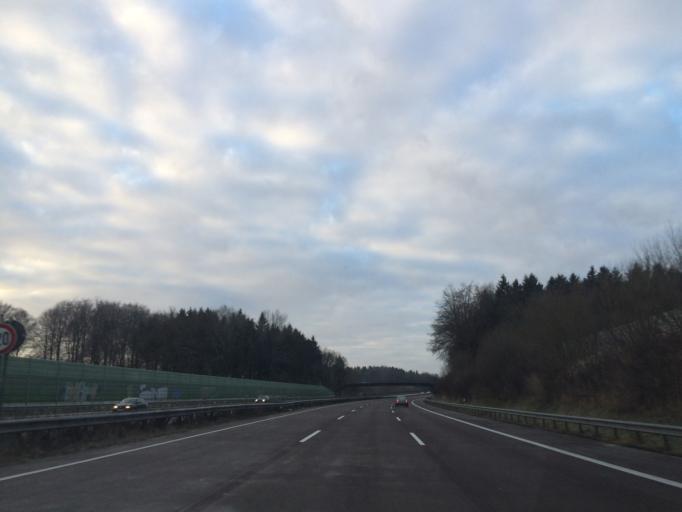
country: DE
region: Schleswig-Holstein
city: Grosshansdorf
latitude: 53.6569
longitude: 10.2965
